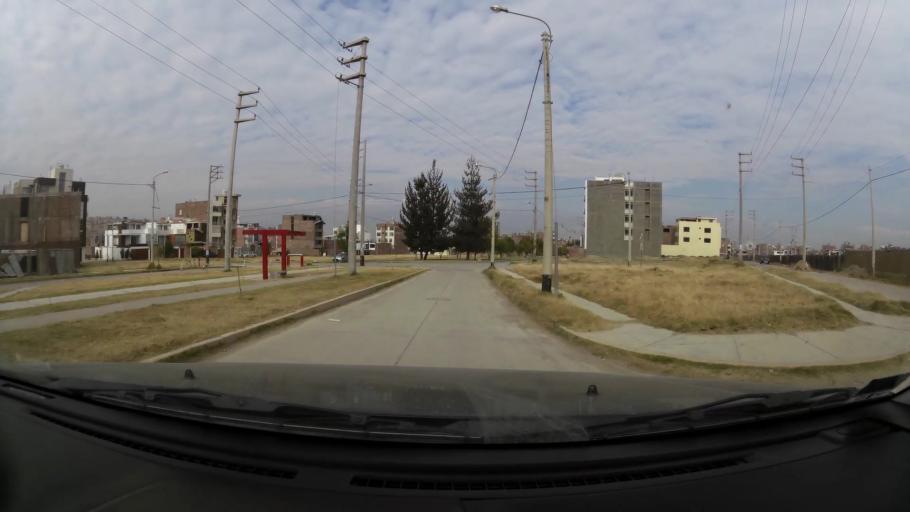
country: PE
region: Junin
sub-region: Provincia de Huancayo
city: Huancayo
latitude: -12.0479
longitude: -75.1890
